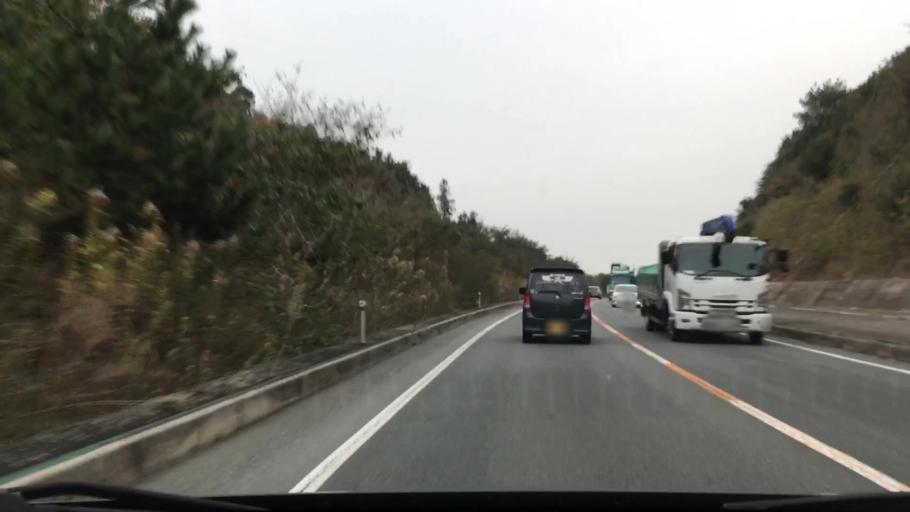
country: JP
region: Yamaguchi
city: Onoda
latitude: 34.0450
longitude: 131.1467
